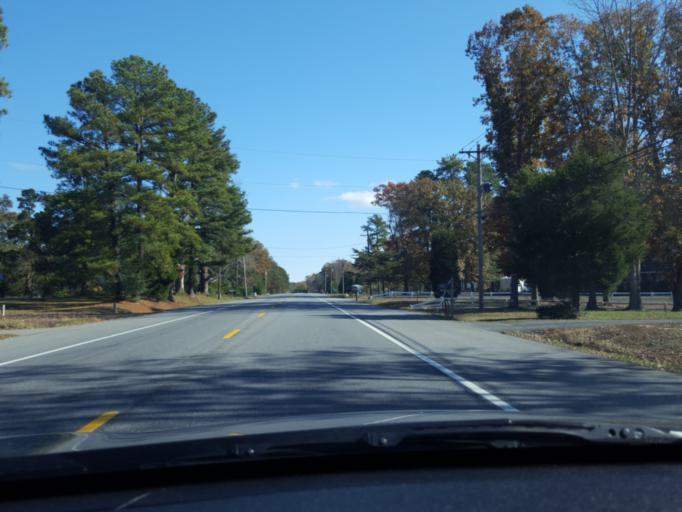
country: US
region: Maryland
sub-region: Saint Mary's County
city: California
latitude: 38.2410
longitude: -76.5598
